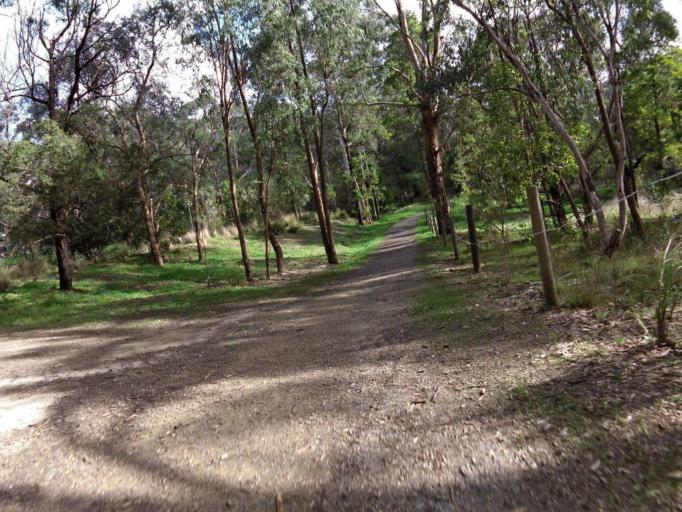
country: AU
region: Victoria
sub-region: Manningham
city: Park Orchards
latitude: -37.7770
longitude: 145.2230
